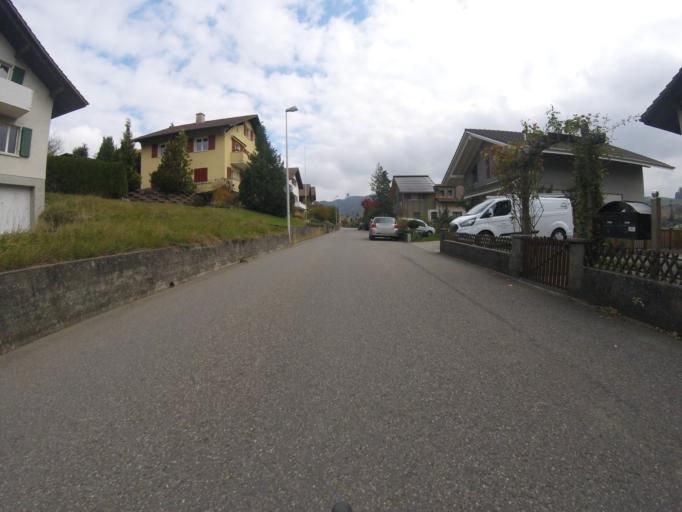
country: CH
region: Bern
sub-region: Bern-Mittelland District
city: Koniz
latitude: 46.8978
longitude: 7.3970
